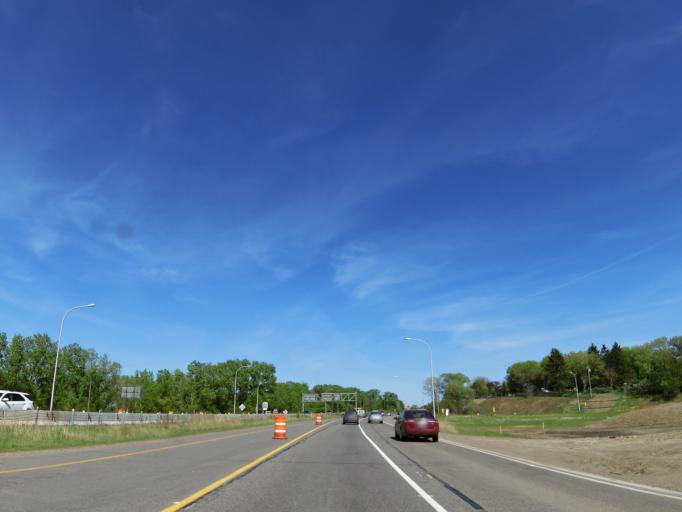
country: US
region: Minnesota
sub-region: Ramsey County
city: Little Canada
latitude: 45.0106
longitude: -93.0886
